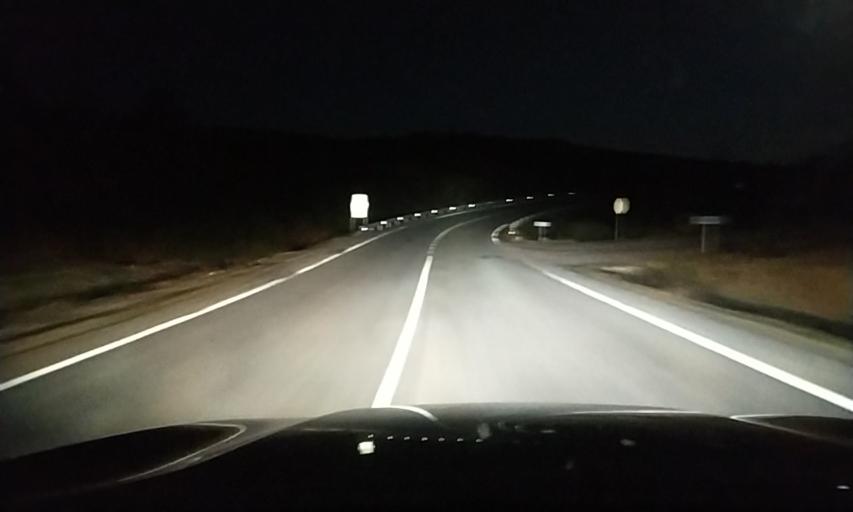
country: ES
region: Galicia
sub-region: Provincia de Ourense
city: Cualedro
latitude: 41.9807
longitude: -7.5331
